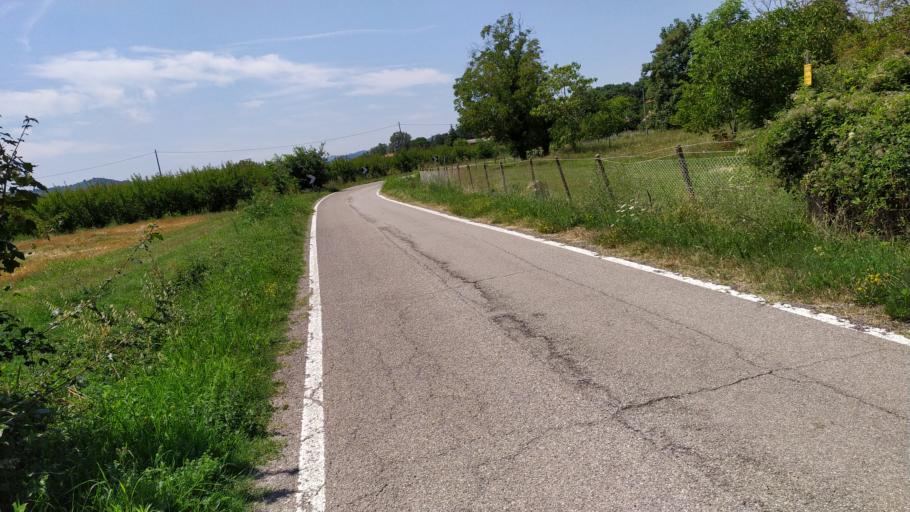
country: IT
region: Emilia-Romagna
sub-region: Forli-Cesena
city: Castrocaro Terme e Terra del Sole
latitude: 44.2010
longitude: 11.9867
